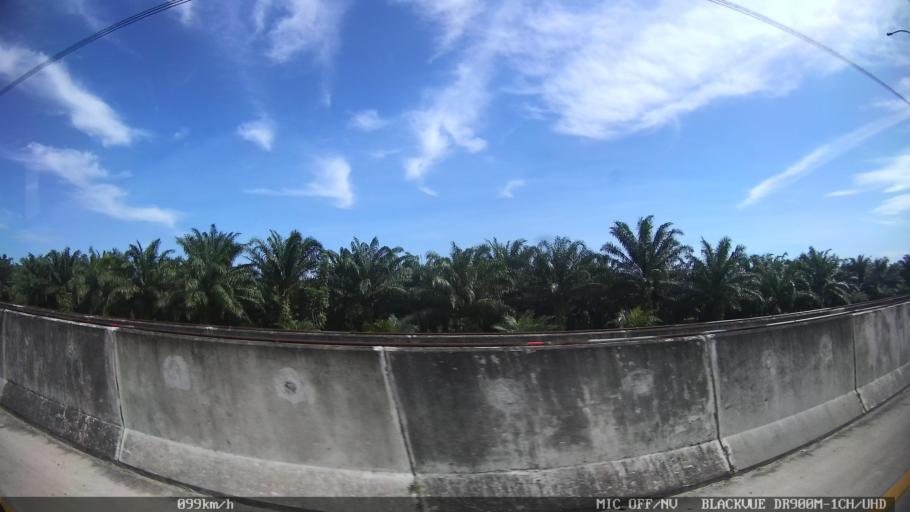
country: ID
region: North Sumatra
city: Sunggal
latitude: 3.6385
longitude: 98.6085
